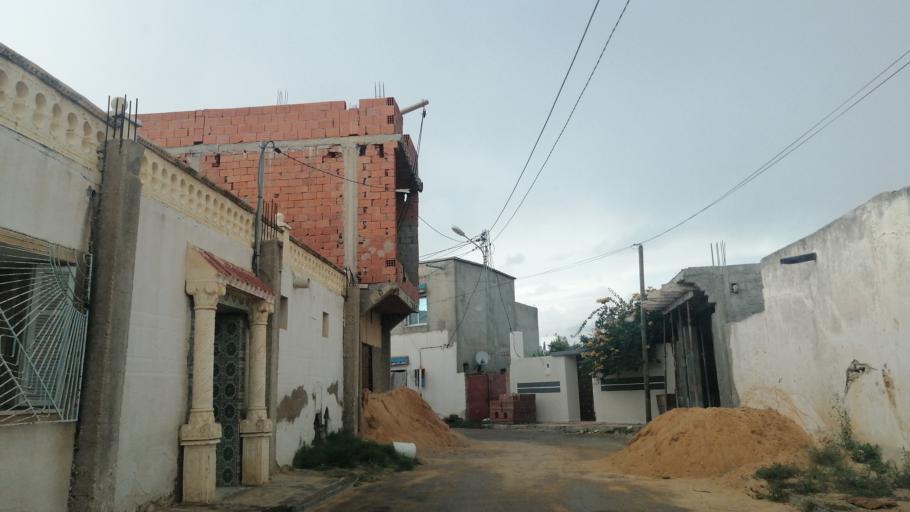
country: TN
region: Al Qayrawan
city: Sbikha
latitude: 36.1239
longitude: 10.0920
